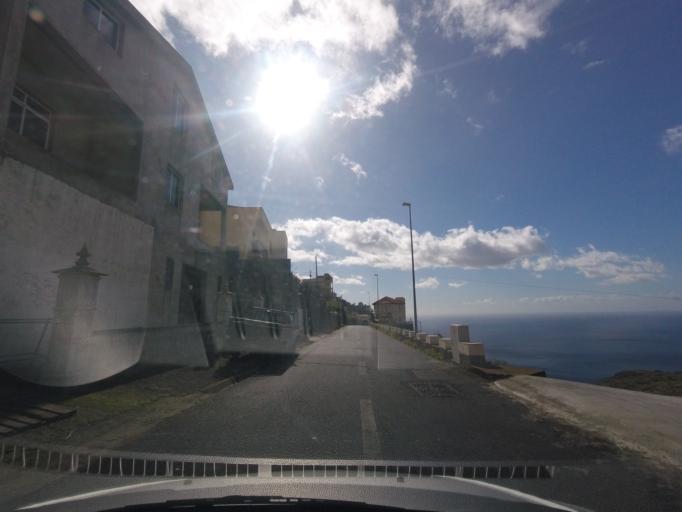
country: PT
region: Madeira
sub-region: Ribeira Brava
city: Campanario
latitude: 32.6622
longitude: -17.0195
